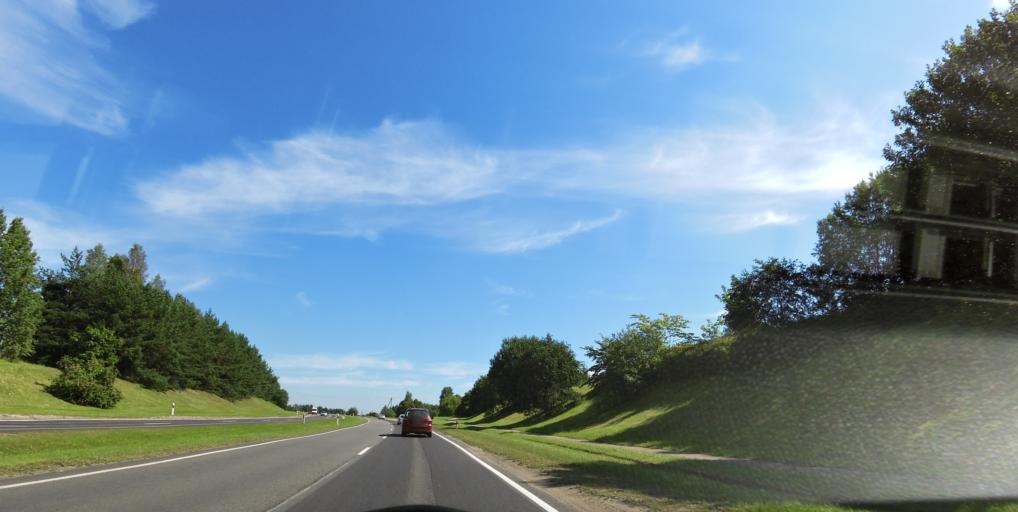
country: LT
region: Vilnius County
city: Rasos
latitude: 54.6900
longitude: 25.3394
